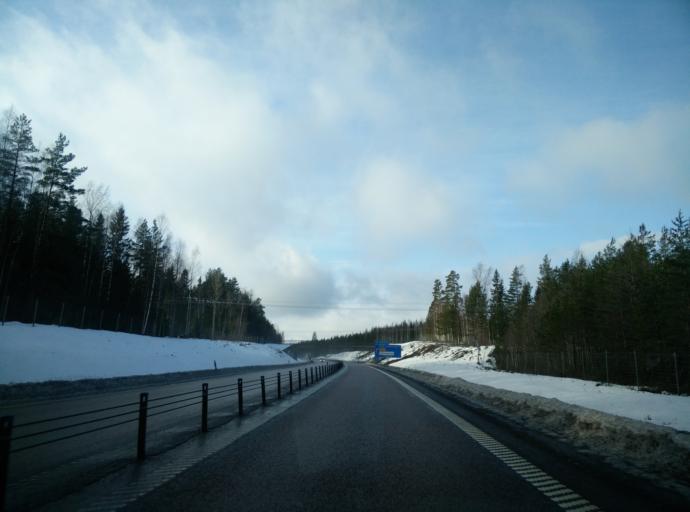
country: SE
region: Gaevleborg
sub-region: Sandvikens Kommun
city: Sandviken
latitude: 60.6276
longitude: 16.7440
